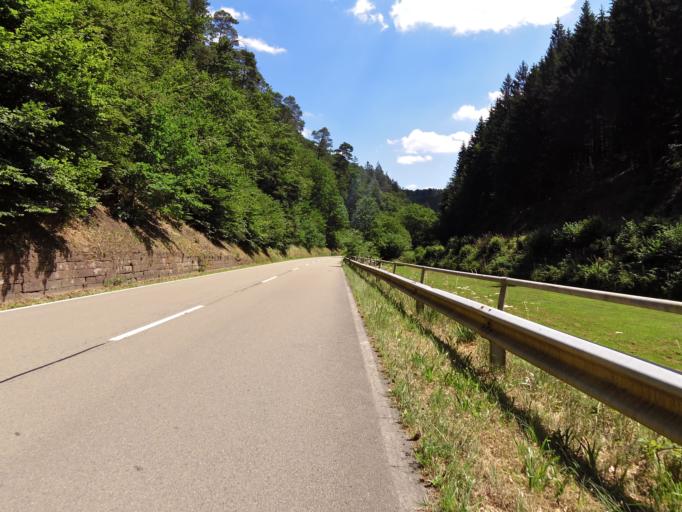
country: DE
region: Rheinland-Pfalz
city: Waldleiningen
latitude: 49.3559
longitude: 7.8886
